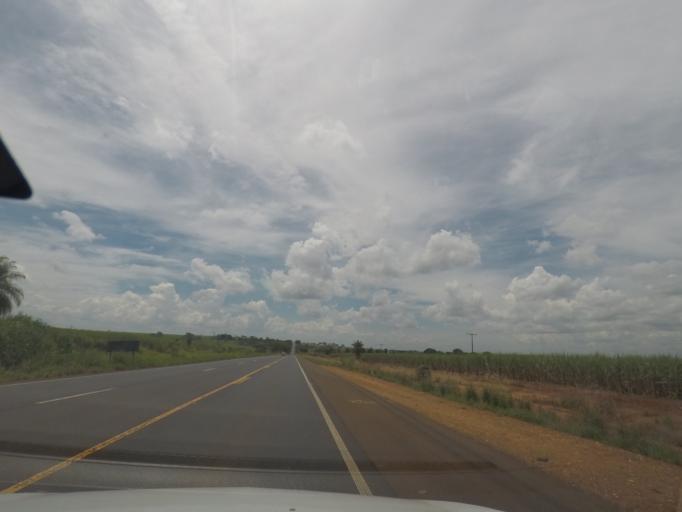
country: BR
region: Sao Paulo
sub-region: Barretos
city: Barretos
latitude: -20.4116
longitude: -48.6334
